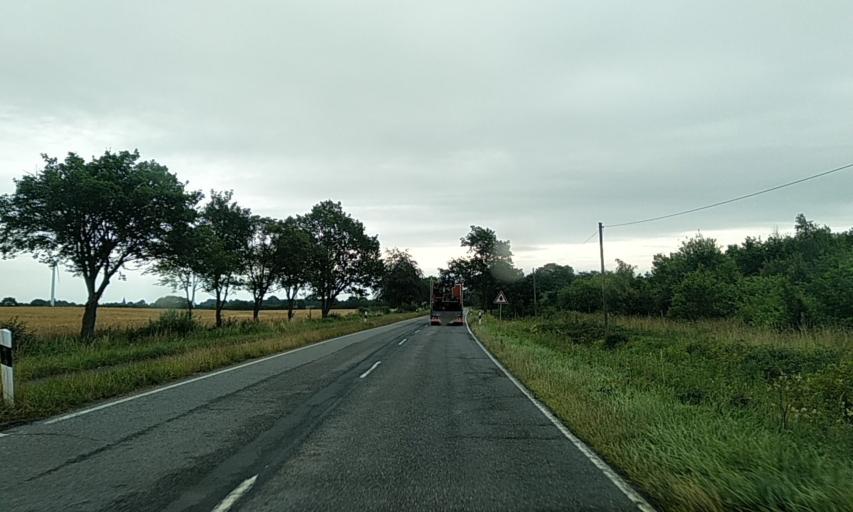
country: DE
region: Schleswig-Holstein
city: Boel
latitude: 54.6403
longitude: 9.6971
